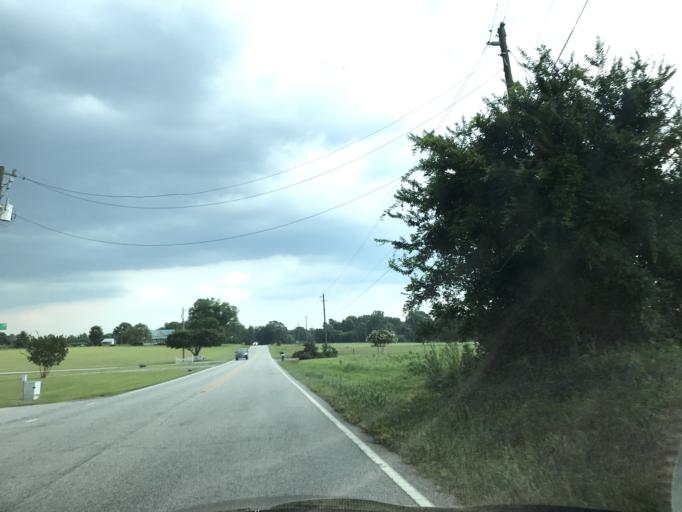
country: US
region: North Carolina
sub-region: Johnston County
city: Four Oaks
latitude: 35.5114
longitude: -78.4788
